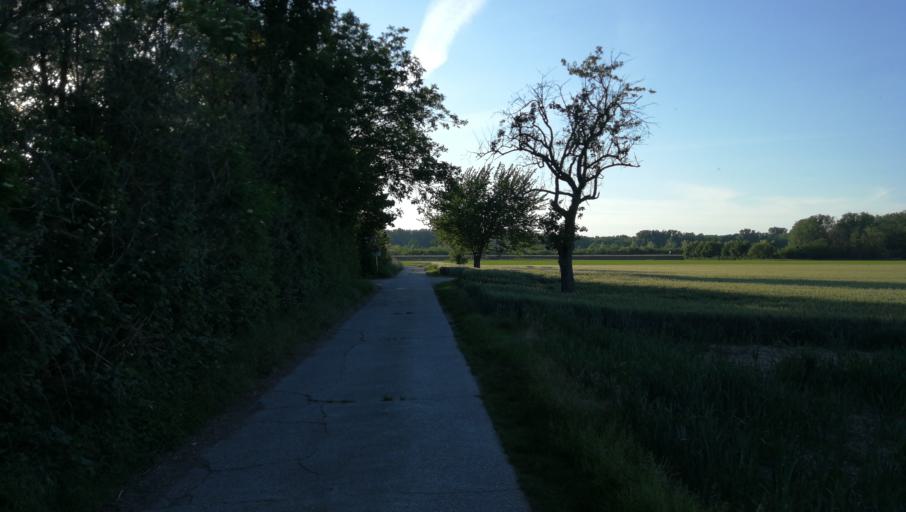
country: DE
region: Baden-Wuerttemberg
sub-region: Karlsruhe Region
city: Ketsch
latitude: 49.3477
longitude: 8.4940
